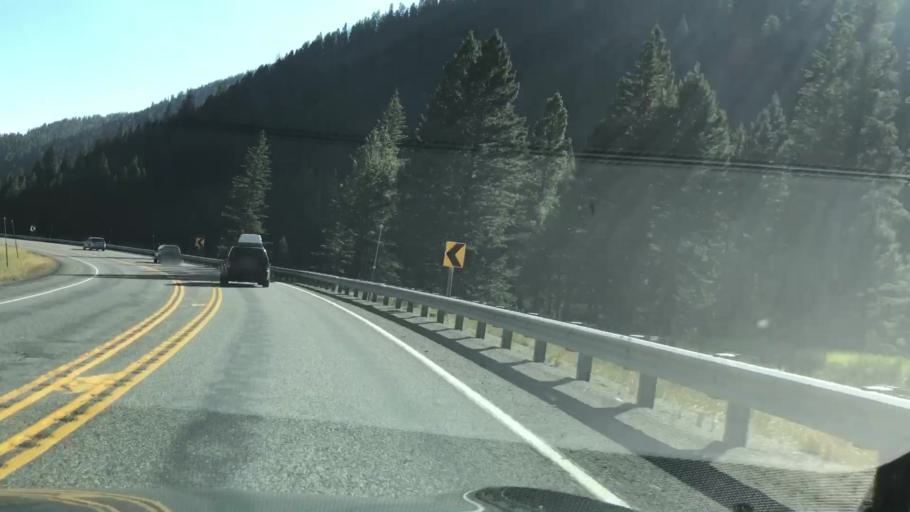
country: US
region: Montana
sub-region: Gallatin County
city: Big Sky
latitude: 45.3752
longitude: -111.1756
